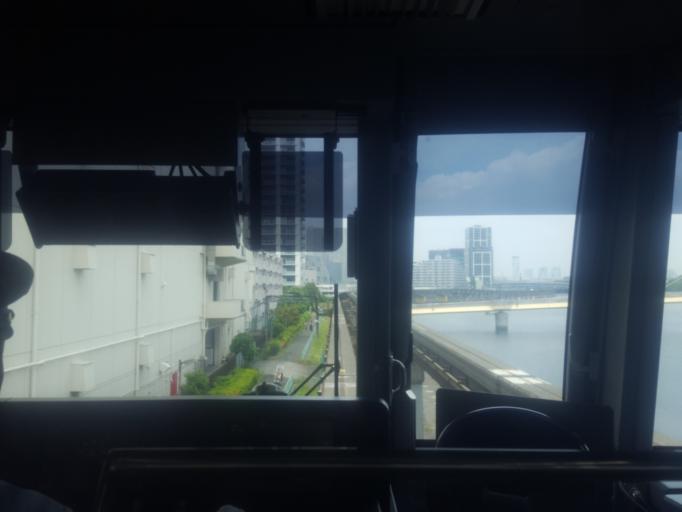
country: JP
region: Kanagawa
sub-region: Kawasaki-shi
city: Kawasaki
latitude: 35.5984
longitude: 139.7472
